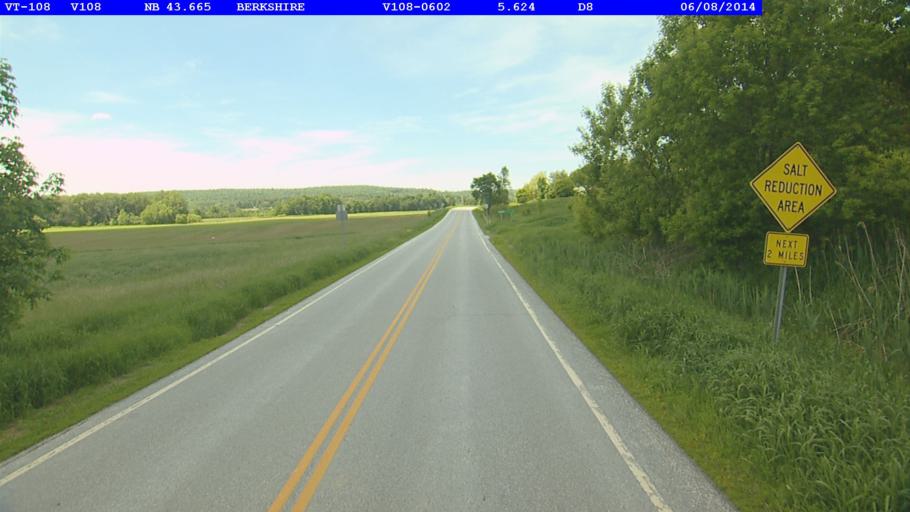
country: US
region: Vermont
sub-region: Franklin County
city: Enosburg Falls
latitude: 44.9983
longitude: -72.8235
